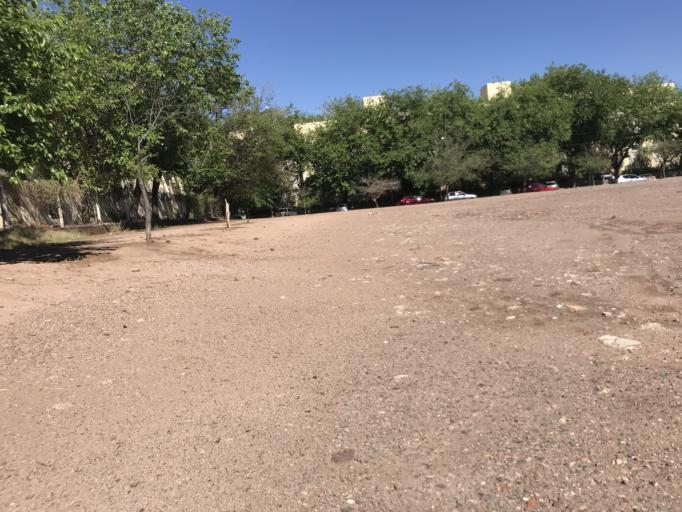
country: AR
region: Mendoza
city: Mendoza
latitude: -32.8762
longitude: -68.8375
